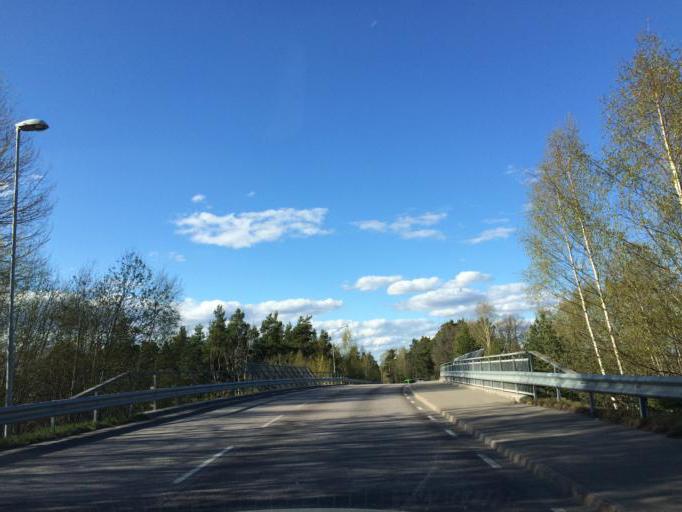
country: SE
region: Soedermanland
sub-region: Eskilstuna Kommun
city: Kvicksund
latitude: 59.4277
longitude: 16.3392
